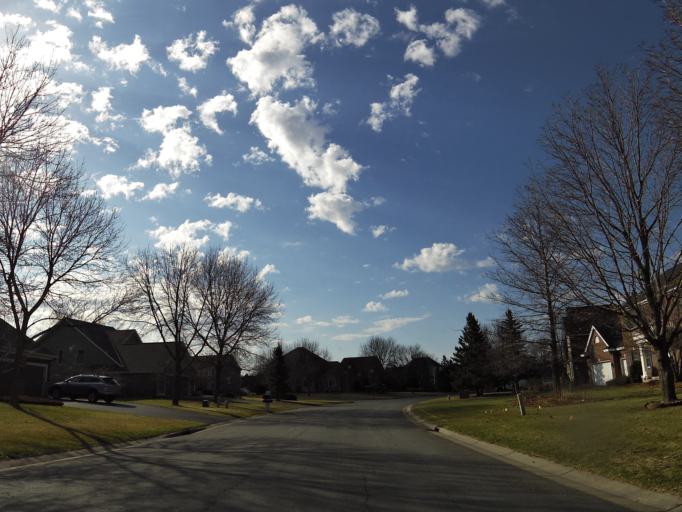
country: US
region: Minnesota
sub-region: Washington County
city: Woodbury
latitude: 44.8981
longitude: -92.8955
